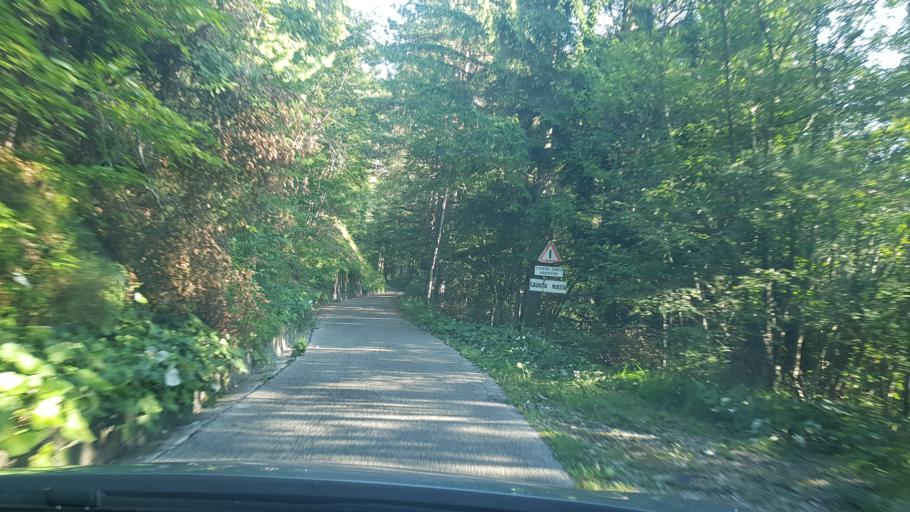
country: IT
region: Friuli Venezia Giulia
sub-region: Provincia di Udine
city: Moggio Udinese
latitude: 46.4387
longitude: 13.2117
